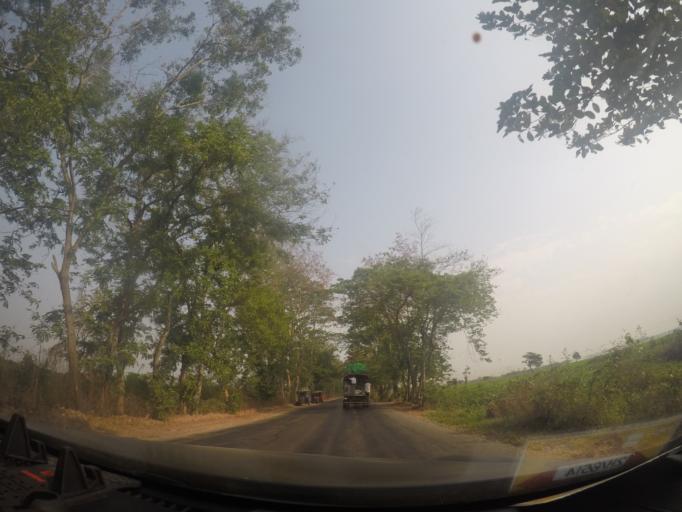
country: MM
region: Bago
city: Paungde
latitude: 18.3752
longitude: 95.5933
